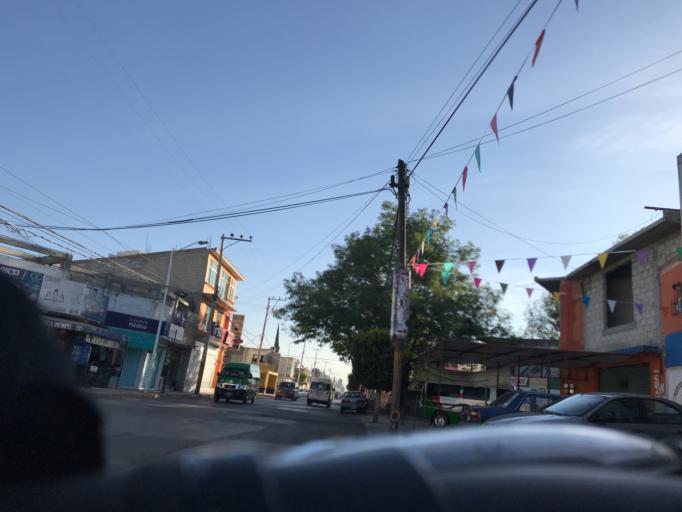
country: MX
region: Mexico
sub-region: Tultepec
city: Tultepec
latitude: 19.6802
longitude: -99.1422
